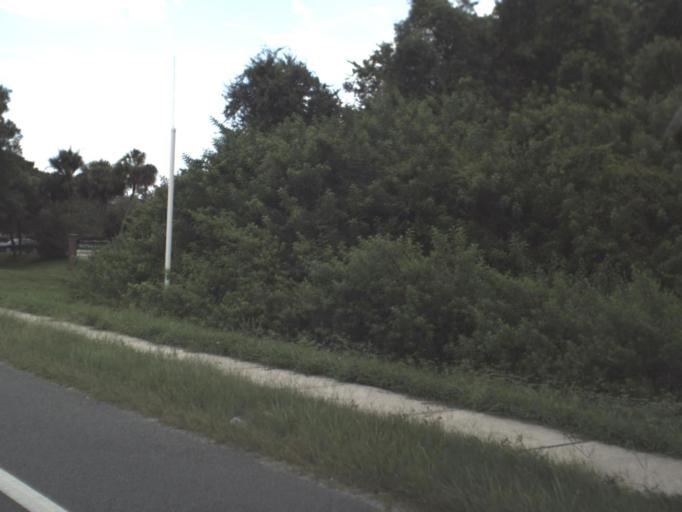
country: US
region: Florida
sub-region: Hillsborough County
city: Carrollwood
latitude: 28.0428
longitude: -82.5050
